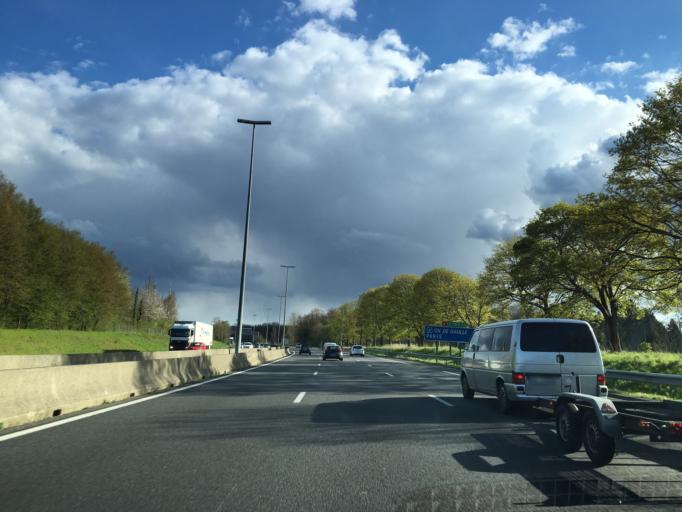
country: FR
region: Picardie
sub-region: Departement de l'Oise
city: Senlis
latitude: 49.1928
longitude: 2.6031
